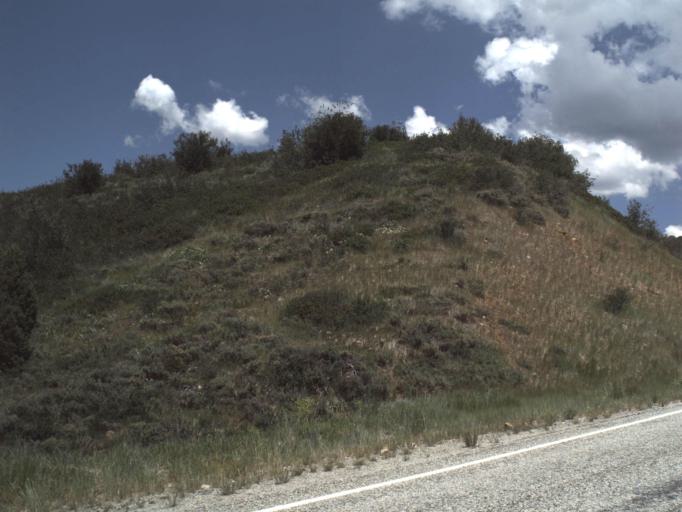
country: US
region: Utah
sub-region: Weber County
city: Wolf Creek
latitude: 41.4098
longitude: -111.5851
